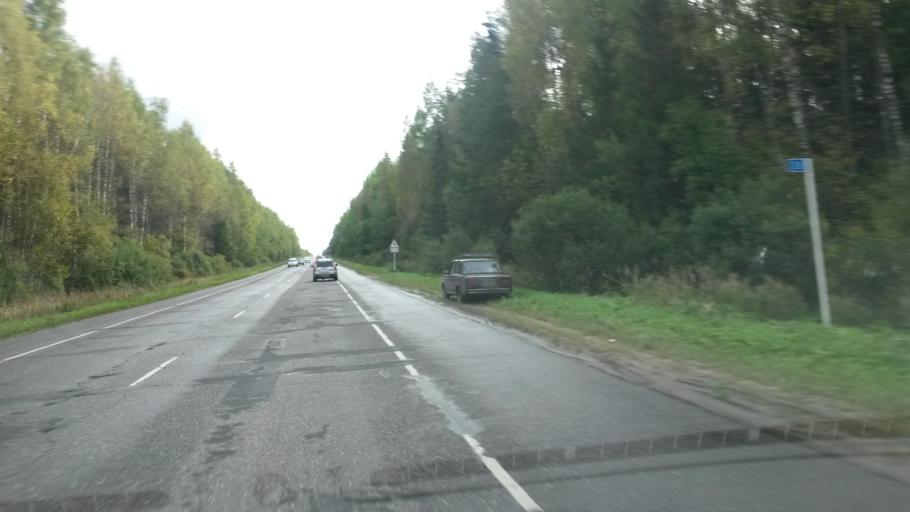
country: RU
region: Ivanovo
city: Kaminskiy
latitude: 57.0750
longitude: 41.4575
